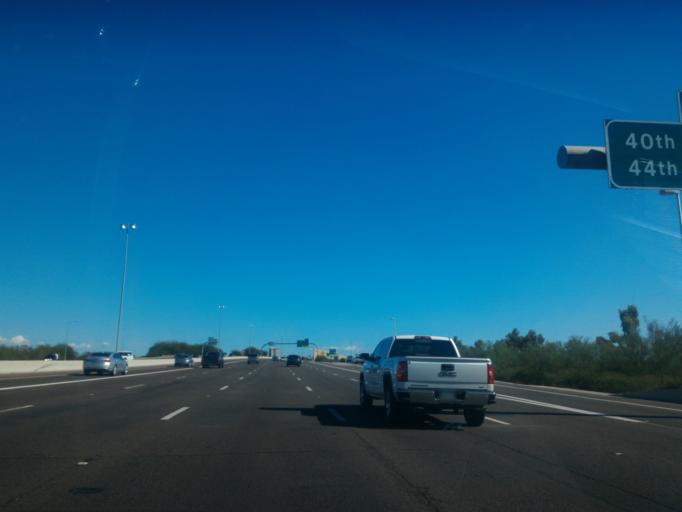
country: US
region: Arizona
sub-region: Maricopa County
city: Tempe Junction
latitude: 33.4590
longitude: -112.0010
